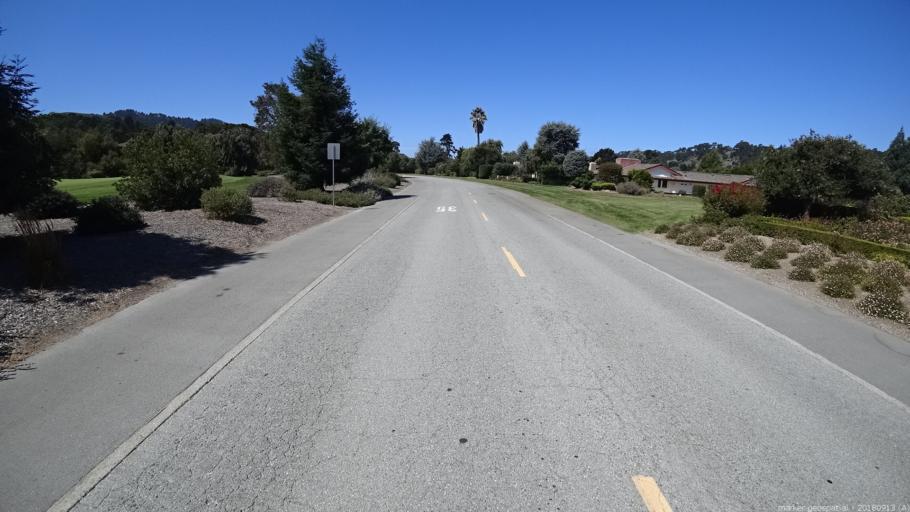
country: US
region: California
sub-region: Monterey County
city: Carmel-by-the-Sea
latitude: 36.5334
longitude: -121.8673
